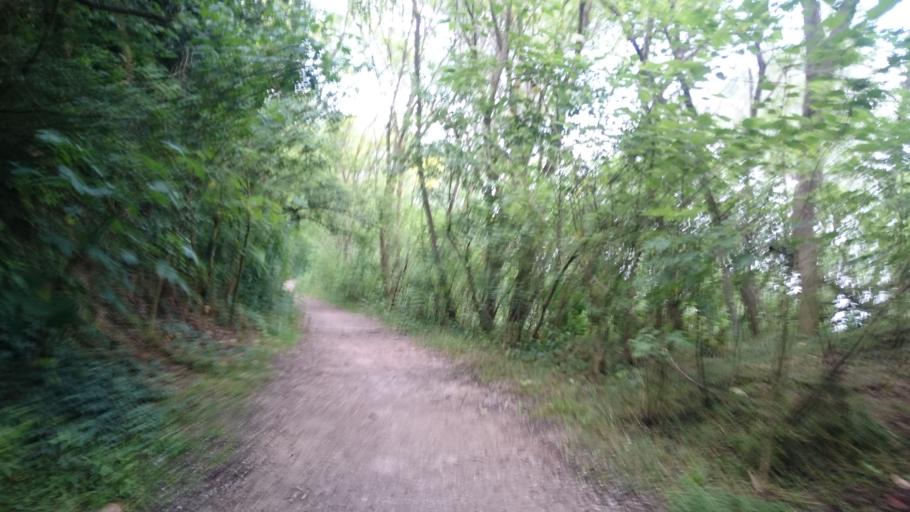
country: IT
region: Lombardy
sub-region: Provincia di Mantova
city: Lunetta-Frassino
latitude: 45.1304
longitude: 10.8168
